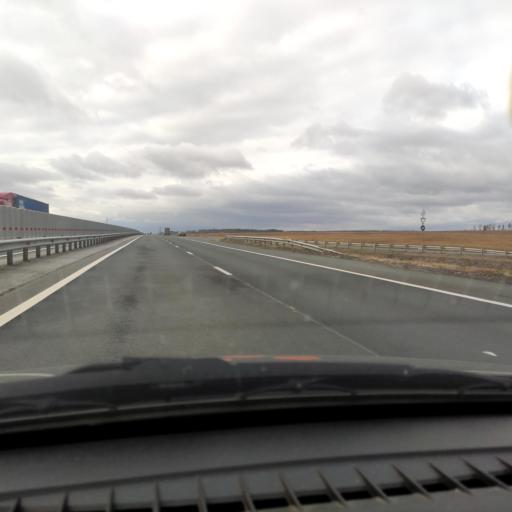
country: RU
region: Samara
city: Bereza
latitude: 53.4684
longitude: 50.1818
